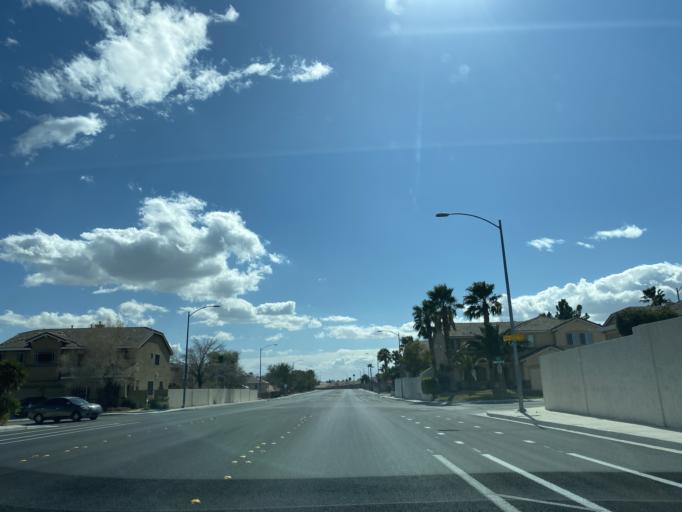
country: US
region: Nevada
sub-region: Clark County
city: Summerlin South
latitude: 36.2308
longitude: -115.3065
